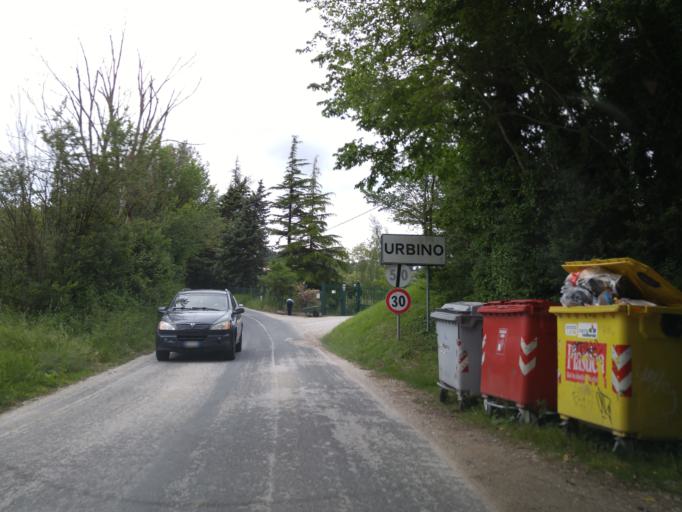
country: IT
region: The Marches
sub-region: Provincia di Pesaro e Urbino
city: Urbino
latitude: 43.7146
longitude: 12.6339
